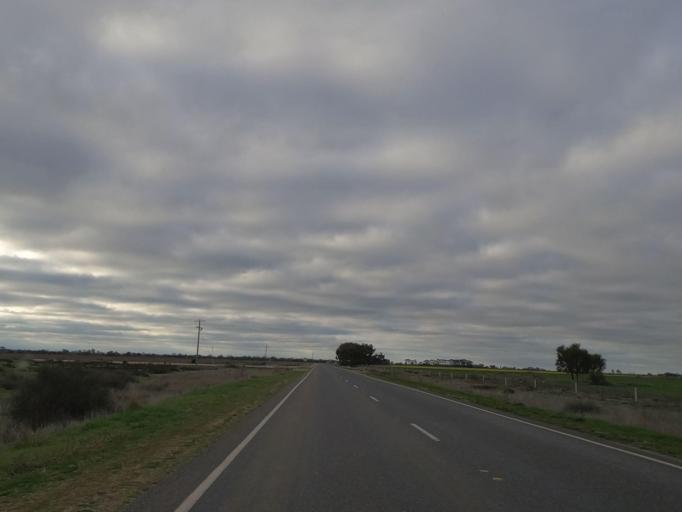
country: AU
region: Victoria
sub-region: Swan Hill
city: Swan Hill
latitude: -35.8327
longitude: 143.9433
